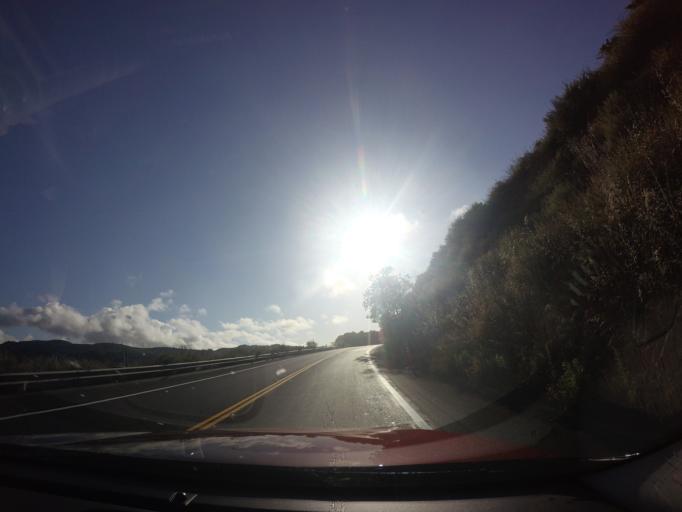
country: US
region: California
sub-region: Monterey County
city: Del Rey Oaks
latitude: 36.5343
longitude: -121.8553
